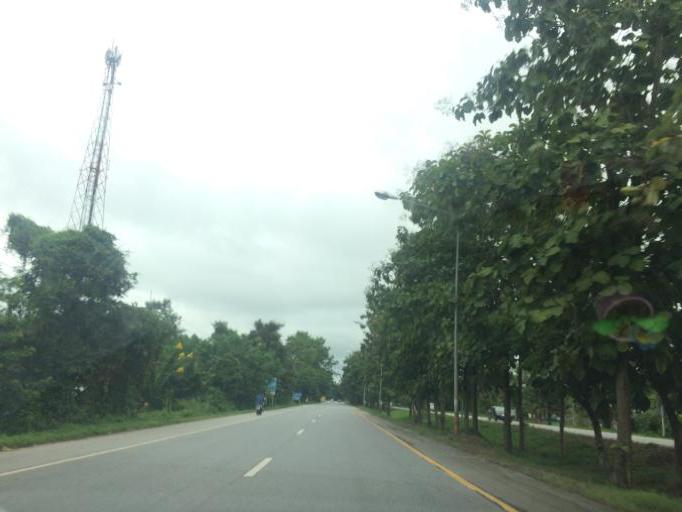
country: TH
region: Chiang Rai
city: Mae Lao
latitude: 19.8029
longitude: 99.7540
